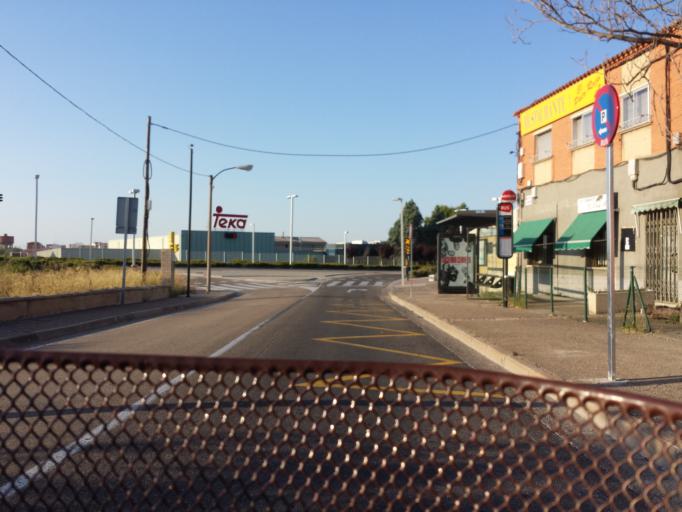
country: ES
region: Aragon
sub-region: Provincia de Zaragoza
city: Oliver-Valdefierro, Oliver, Valdefierro
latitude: 41.6444
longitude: -0.9266
